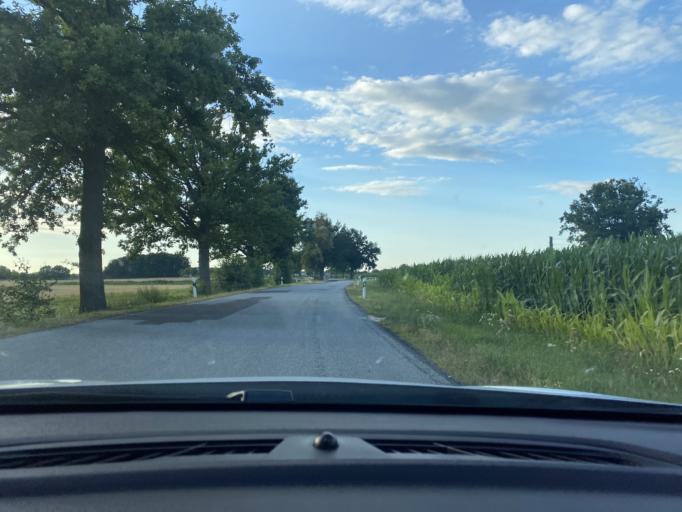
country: DE
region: Saxony
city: Horka
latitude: 51.2705
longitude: 14.8944
